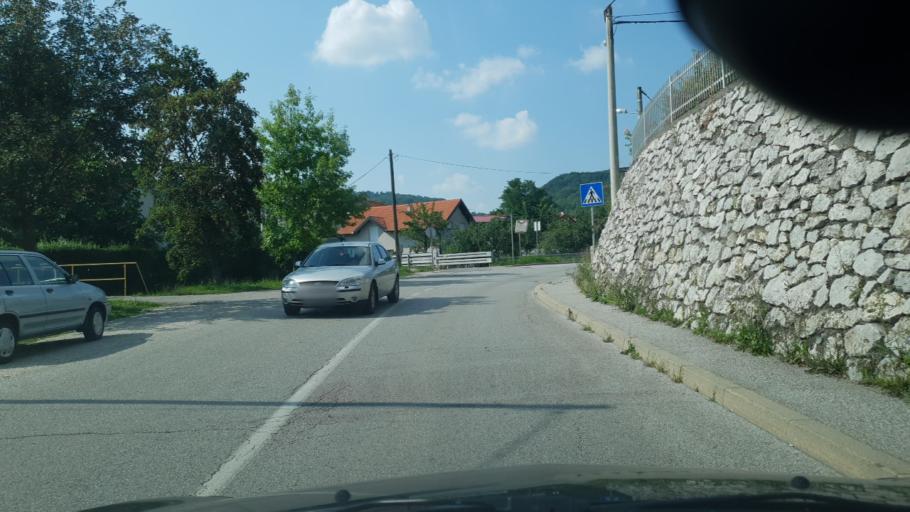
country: HR
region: Grad Zagreb
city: Stenjevec
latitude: 45.8287
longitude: 15.9048
